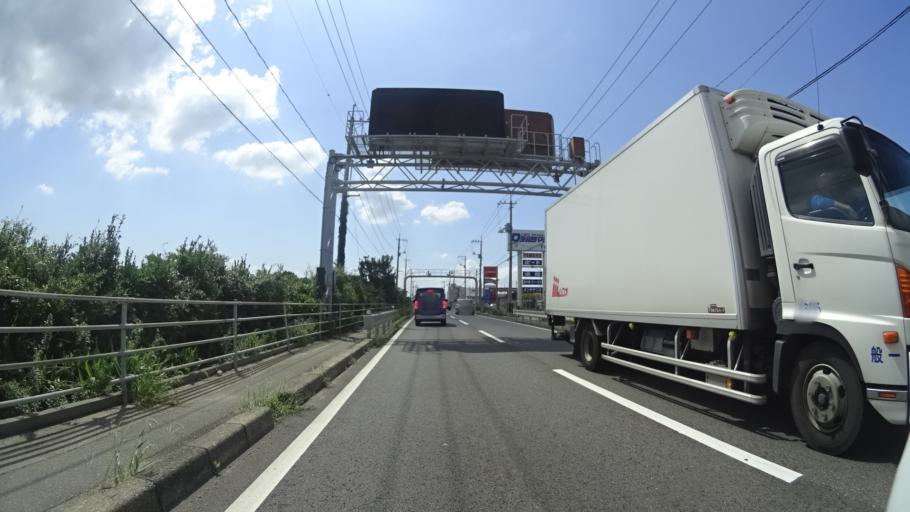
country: JP
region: Yamaguchi
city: Shimonoseki
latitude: 34.0380
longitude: 130.9139
